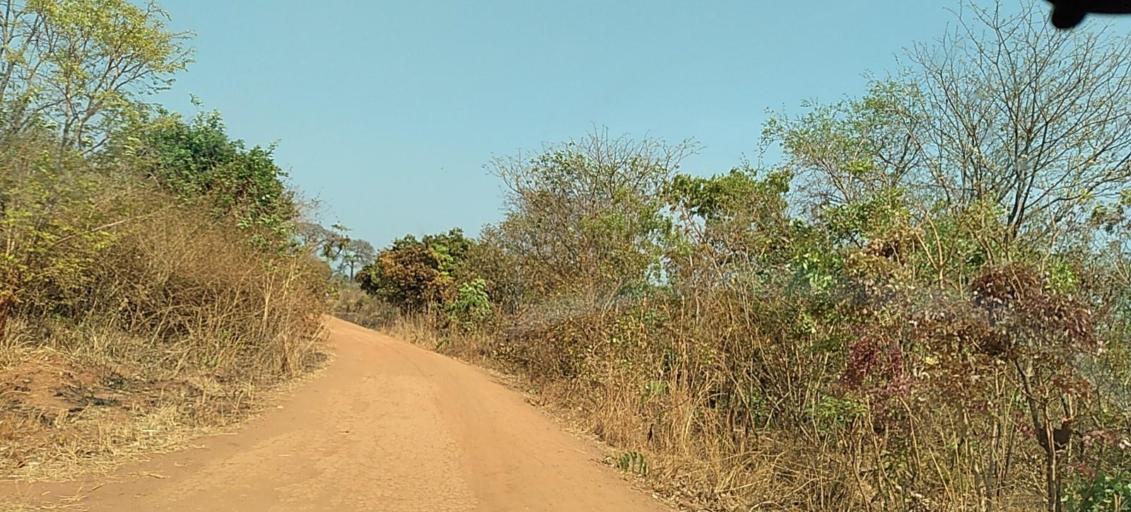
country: ZM
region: North-Western
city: Kasempa
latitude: -13.3894
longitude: 25.6780
